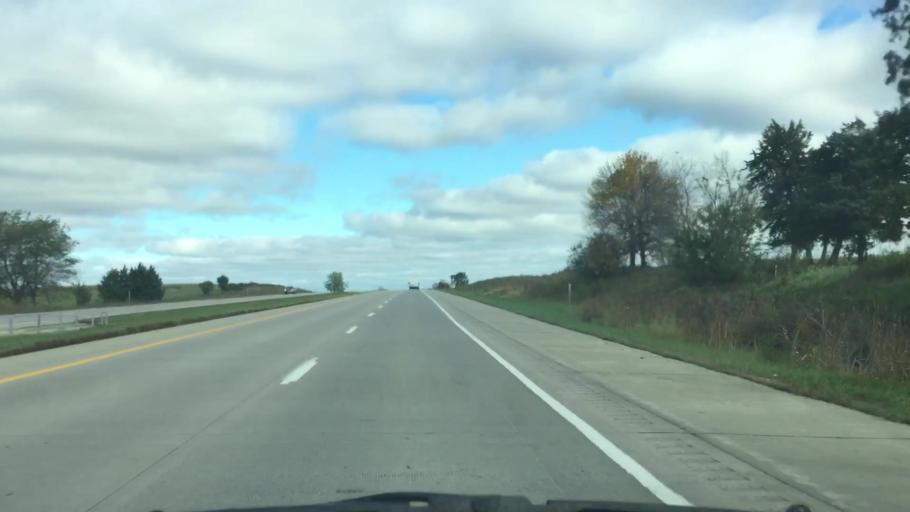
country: US
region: Iowa
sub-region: Clarke County
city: Osceola
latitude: 40.9140
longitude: -93.7972
